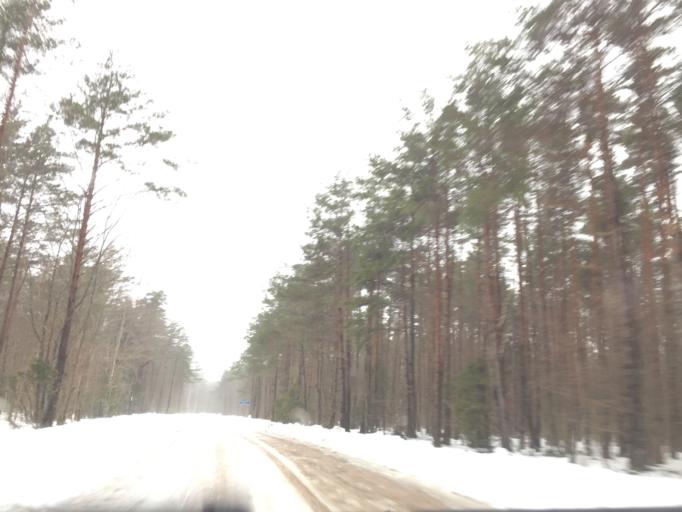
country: EE
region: Saare
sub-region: Kuressaare linn
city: Kuressaare
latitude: 58.2915
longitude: 22.1125
